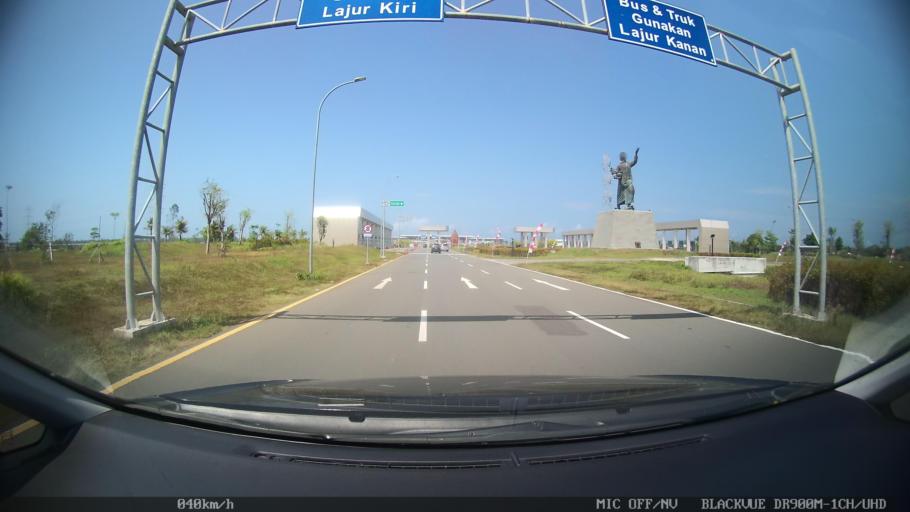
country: ID
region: Daerah Istimewa Yogyakarta
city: Srandakan
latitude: -7.8869
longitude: 110.0644
